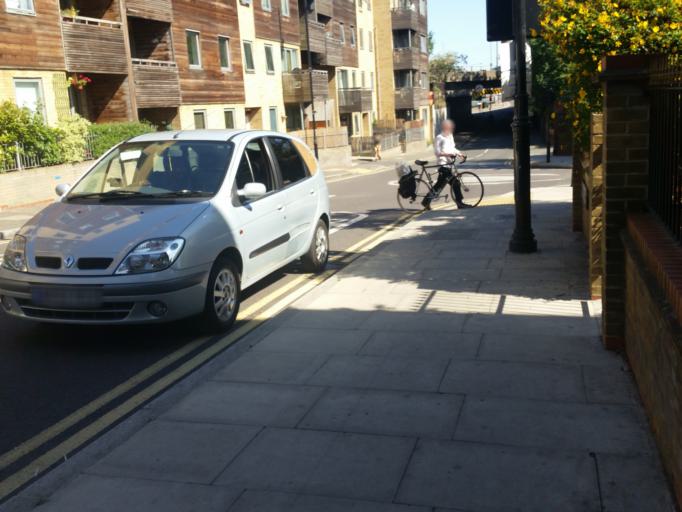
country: GB
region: England
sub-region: Greater London
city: Hackney
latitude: 51.5392
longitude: -0.0270
